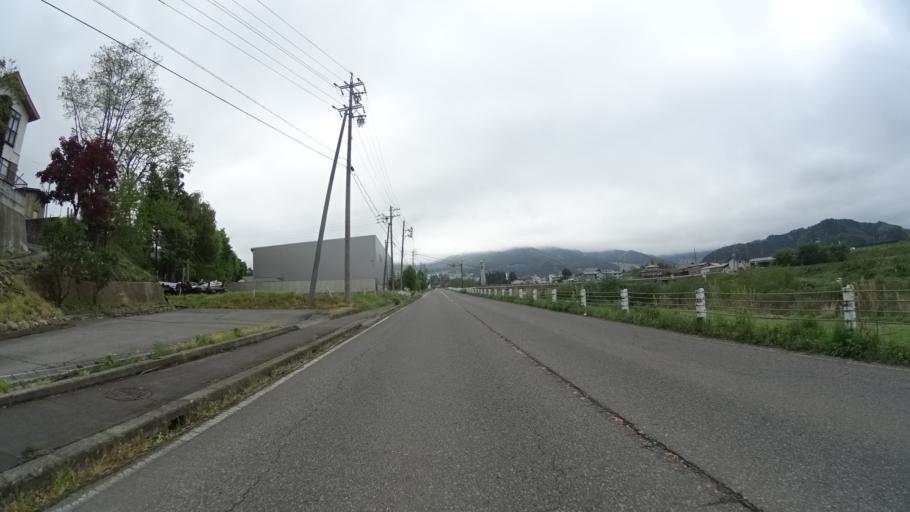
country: JP
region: Nagano
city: Nakano
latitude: 36.7475
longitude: 138.4038
